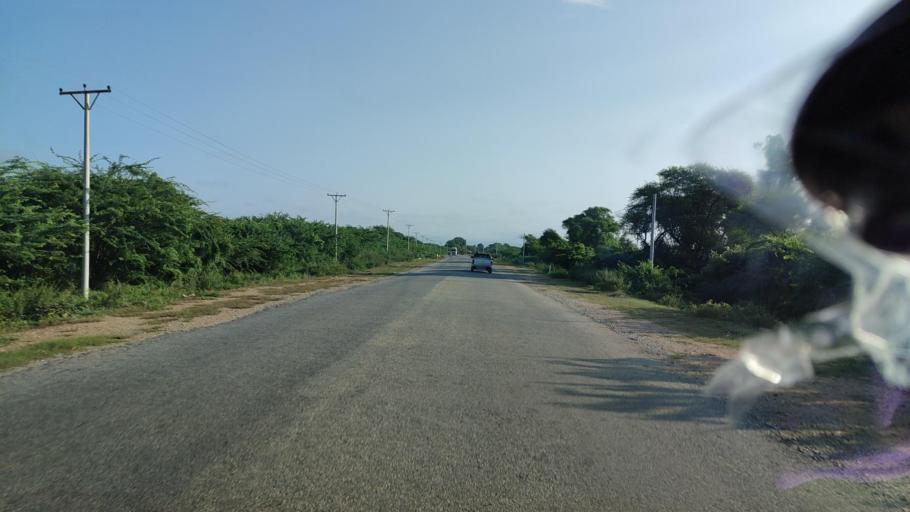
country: MM
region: Mandalay
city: Yamethin
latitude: 20.6613
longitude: 96.1190
